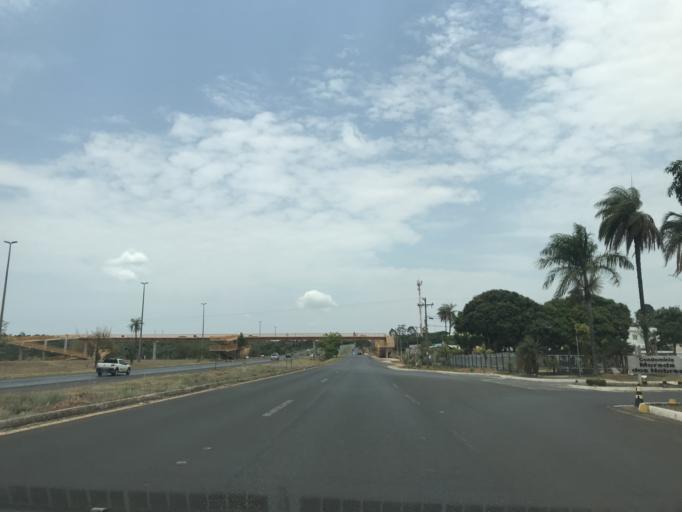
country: BR
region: Federal District
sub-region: Brasilia
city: Brasilia
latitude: -15.6741
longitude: -47.8222
